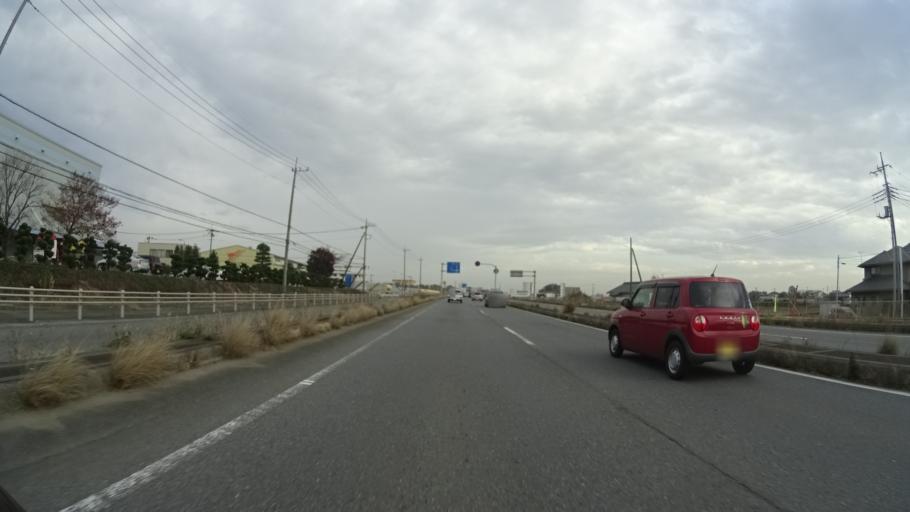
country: JP
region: Gunma
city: Isesaki
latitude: 36.3645
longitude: 139.1805
